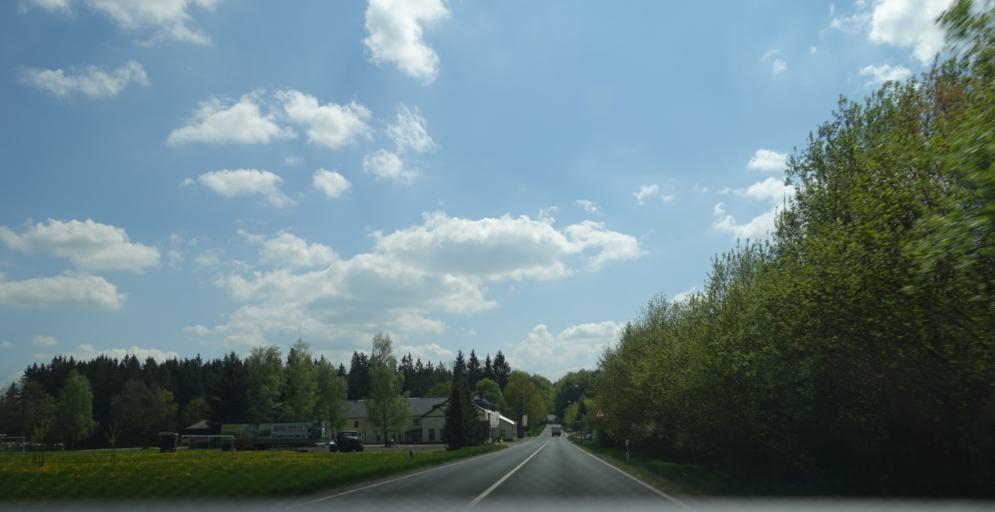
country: DE
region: Saxony
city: Grosshartmannsdorf
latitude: 50.8310
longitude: 13.3250
